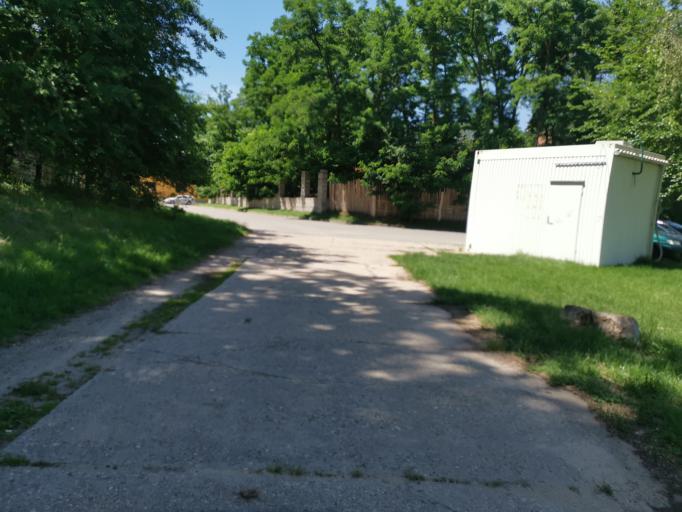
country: CZ
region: South Moravian
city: Vracov
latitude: 48.9687
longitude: 17.2214
